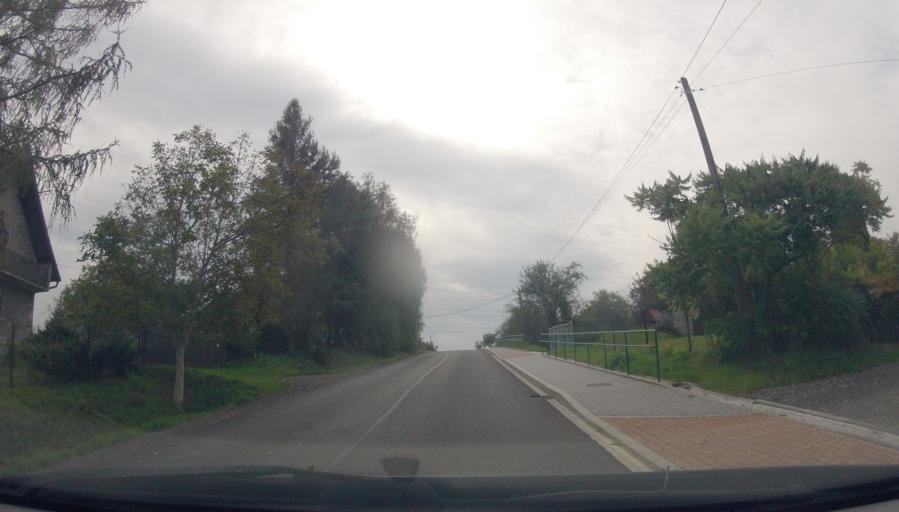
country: PL
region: Lesser Poland Voivodeship
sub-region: Powiat krakowski
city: Ochojno
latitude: 49.9460
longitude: 20.0078
